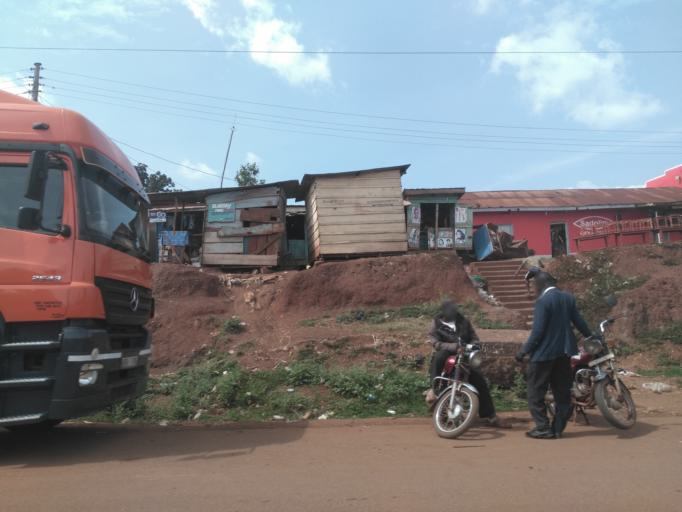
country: UG
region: Eastern Region
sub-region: Jinja District
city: Bugembe
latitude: 0.4671
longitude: 33.2405
